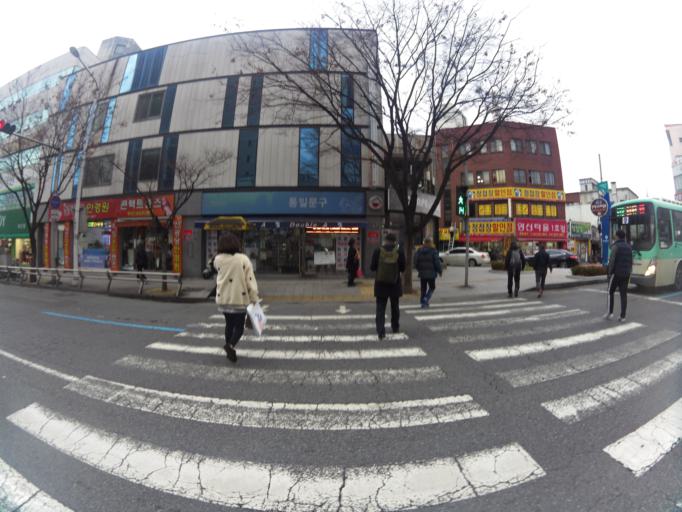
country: KR
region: Daegu
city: Daegu
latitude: 35.8705
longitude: 128.5846
